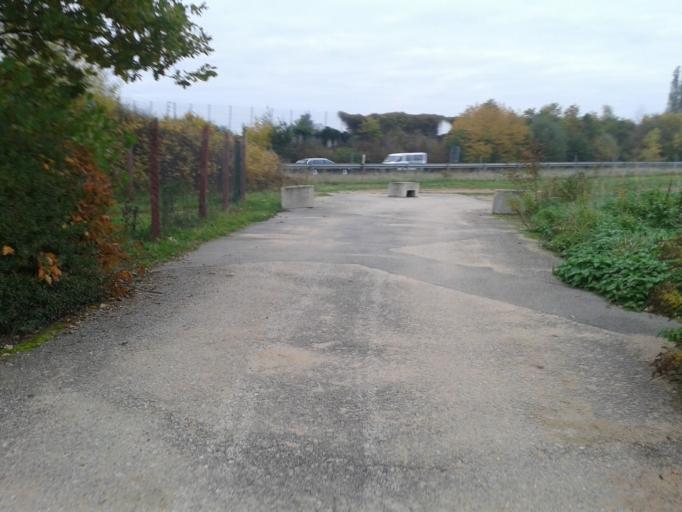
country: DE
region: Bavaria
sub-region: Upper Franconia
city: Gundelsheim
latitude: 49.9260
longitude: 10.9199
